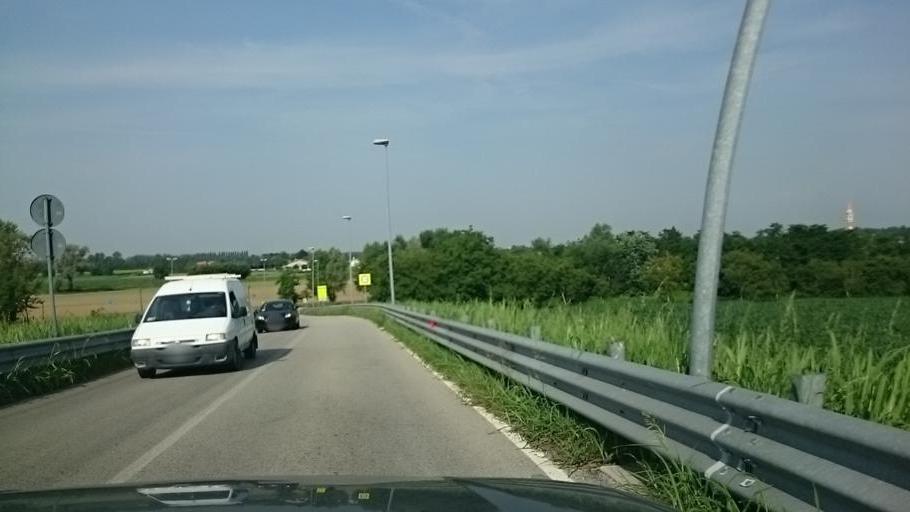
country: IT
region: Veneto
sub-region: Provincia di Treviso
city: Sant'Andrea
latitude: 45.6504
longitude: 11.9186
